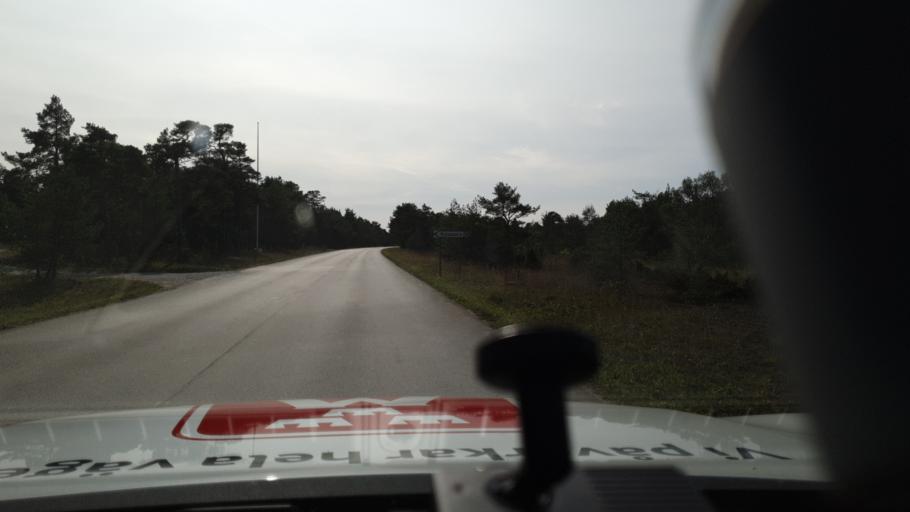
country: SE
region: Gotland
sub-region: Gotland
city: Slite
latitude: 57.8859
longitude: 19.0892
